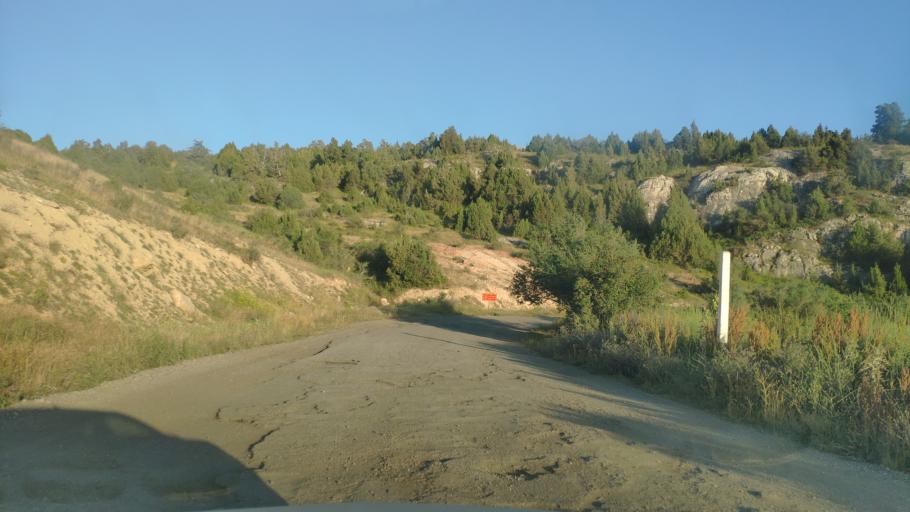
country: TJ
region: Viloyati Sughd
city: Ayni
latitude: 39.6347
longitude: 68.4634
